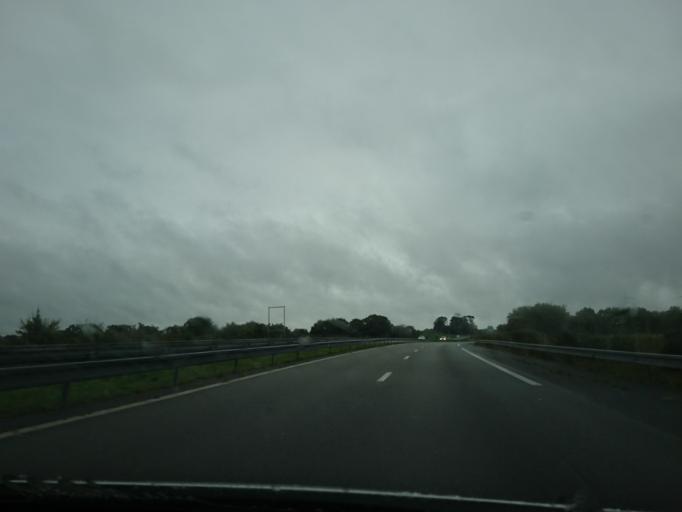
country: FR
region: Brittany
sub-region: Departement du Morbihan
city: Ambon
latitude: 47.5922
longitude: -2.5595
